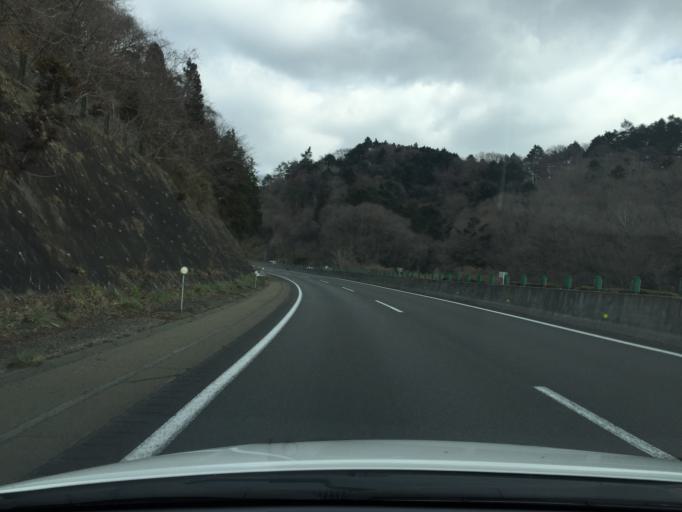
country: JP
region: Miyagi
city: Sendai
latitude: 38.2391
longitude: 140.8181
